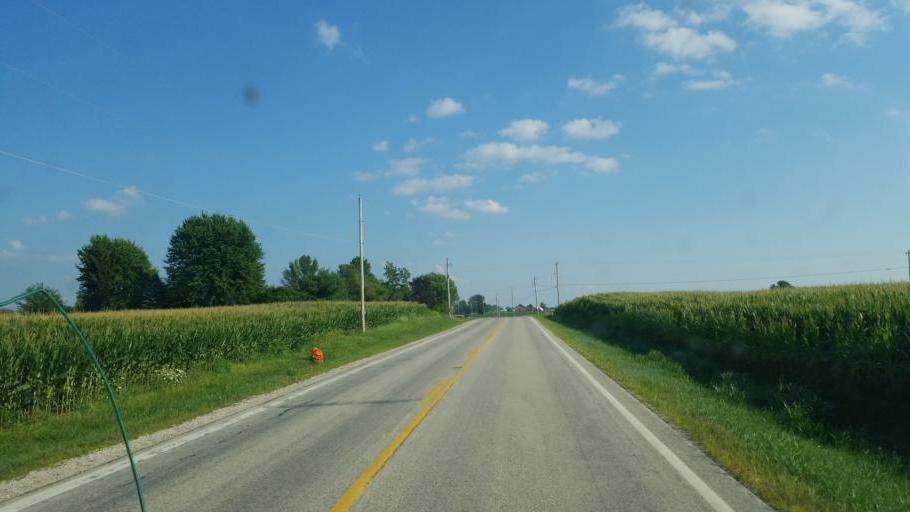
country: US
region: Ohio
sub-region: Crawford County
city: Bucyrus
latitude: 40.8789
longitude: -83.0093
